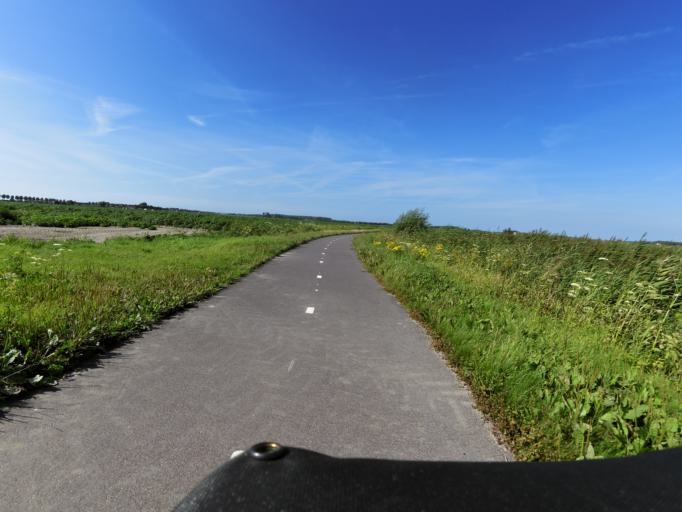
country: NL
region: South Holland
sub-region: Gemeente Goeree-Overflakkee
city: Dirksland
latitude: 51.7459
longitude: 4.0758
